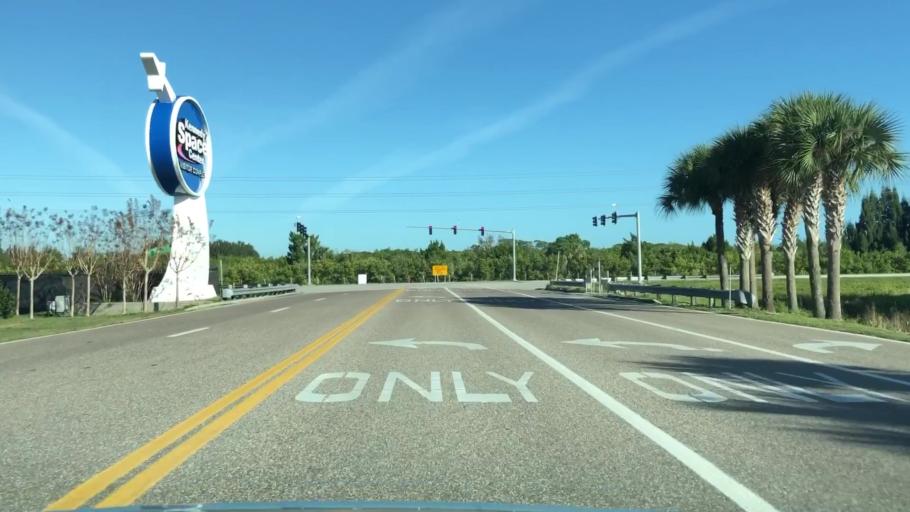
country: US
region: Florida
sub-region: Brevard County
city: Merritt Island
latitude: 28.5254
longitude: -80.6792
